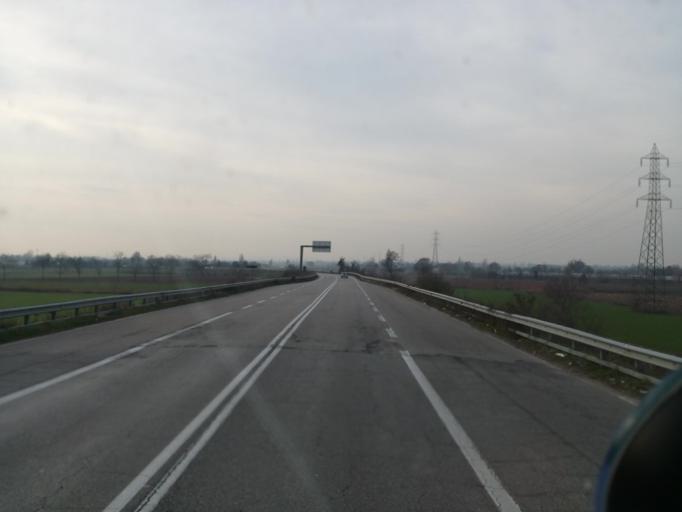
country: IT
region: Lombardy
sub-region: Provincia di Mantova
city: Castiglione delle Stiviere
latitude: 45.4120
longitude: 10.4770
